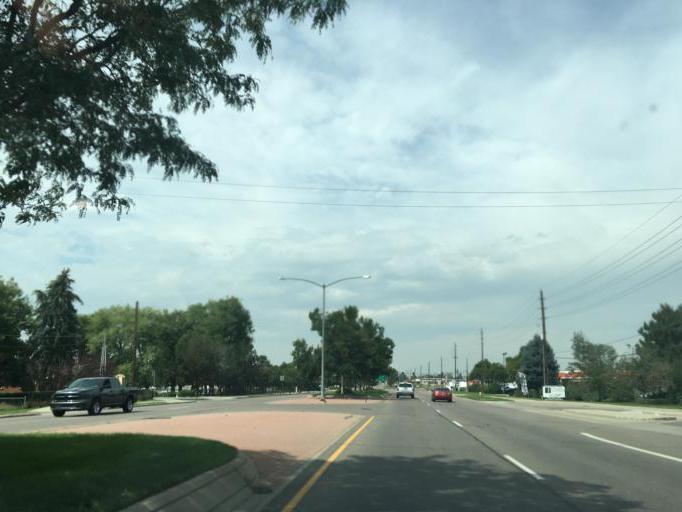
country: US
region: Colorado
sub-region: Adams County
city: Aurora
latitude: 39.7405
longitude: -104.7979
